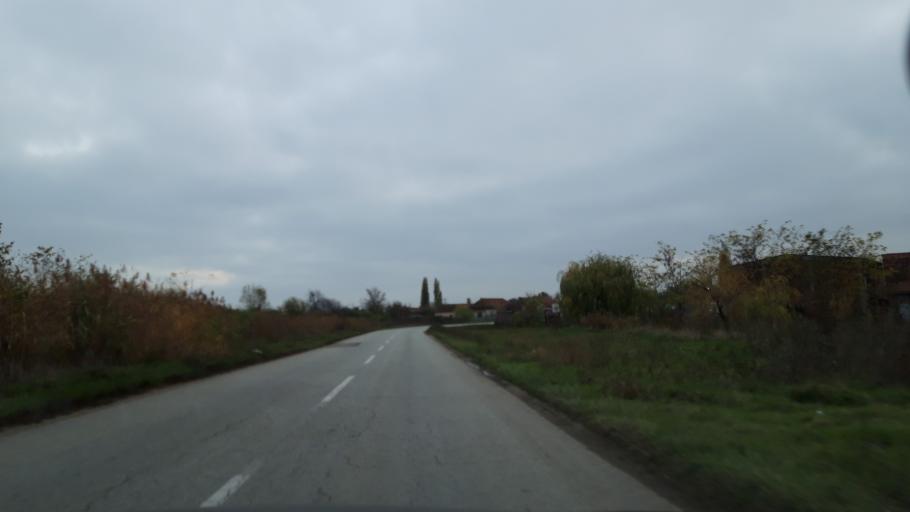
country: RS
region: Autonomna Pokrajina Vojvodina
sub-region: Severnobanatski Okrug
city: Novi Knezevac
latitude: 46.0472
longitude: 20.1038
